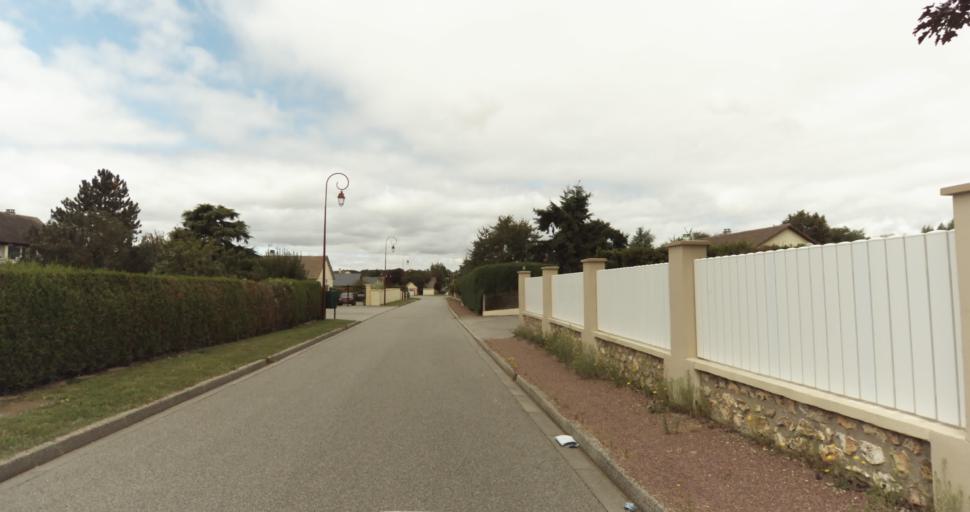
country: FR
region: Haute-Normandie
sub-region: Departement de l'Eure
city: Evreux
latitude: 48.9465
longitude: 1.1798
